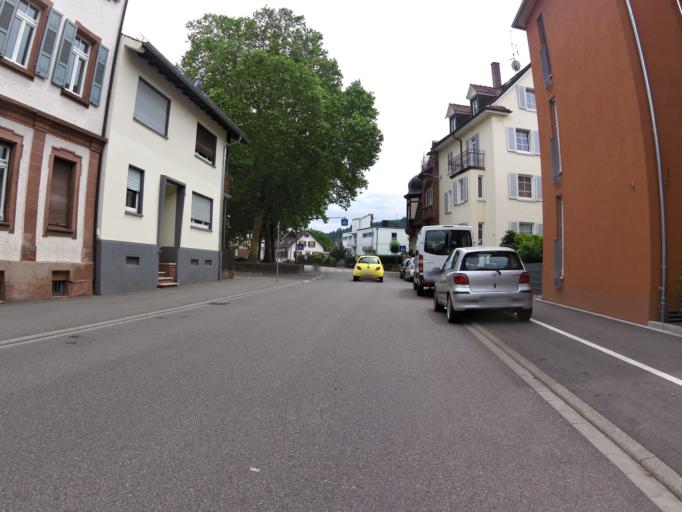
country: DE
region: Baden-Wuerttemberg
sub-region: Freiburg Region
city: Lahr
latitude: 48.3426
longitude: 7.8804
